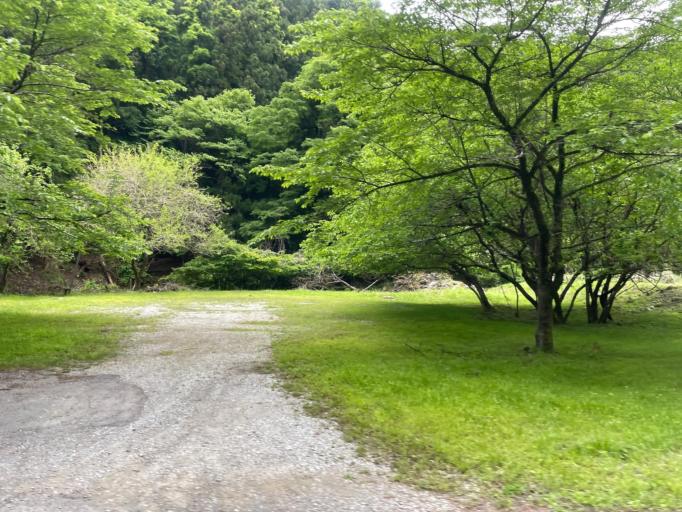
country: JP
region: Tochigi
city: Tanuma
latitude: 36.4666
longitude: 139.5987
